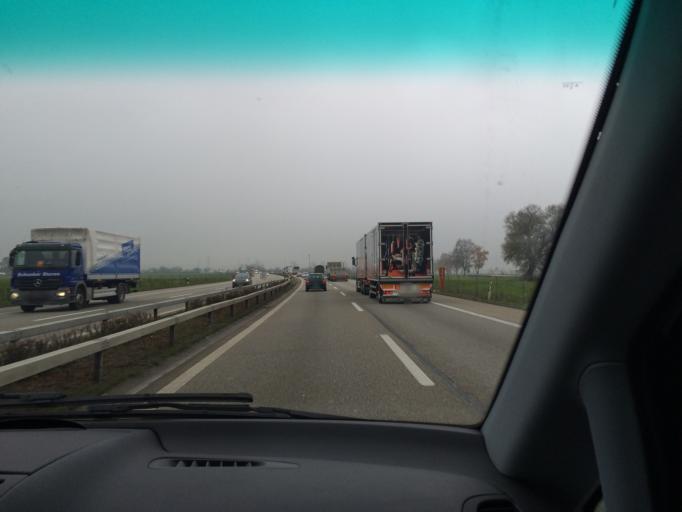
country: CH
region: Solothurn
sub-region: Bezirk Gaeu
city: Oensingen
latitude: 47.2799
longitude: 7.7201
